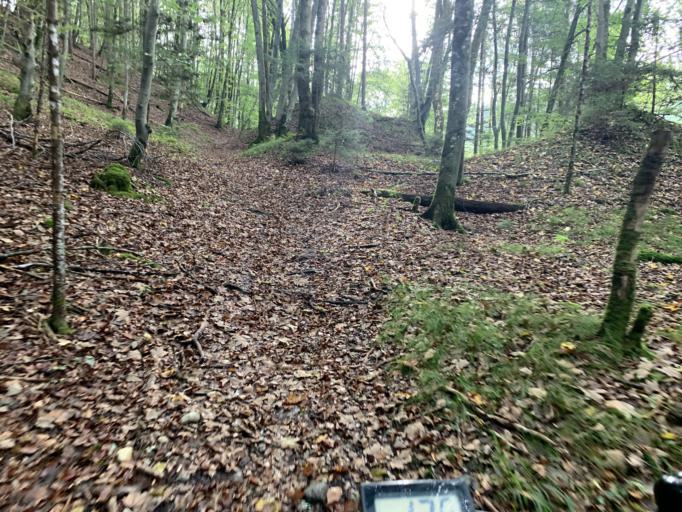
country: DE
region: Bavaria
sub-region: Upper Bavaria
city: Baierbrunn
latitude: 48.0088
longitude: 11.4833
